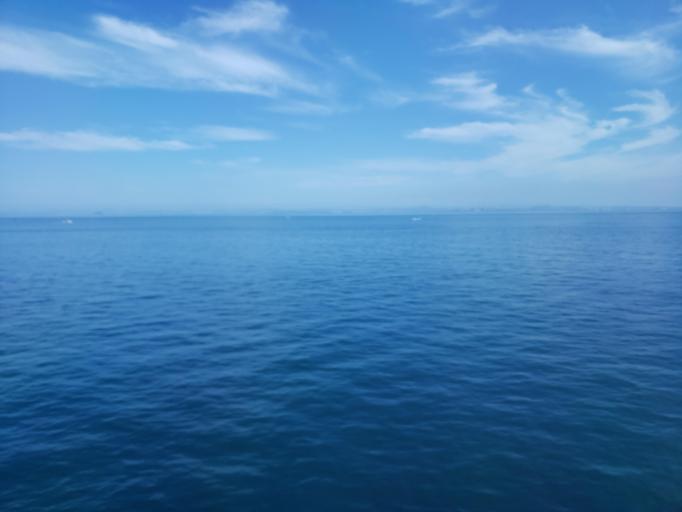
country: JP
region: Hyogo
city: Akashi
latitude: 34.5735
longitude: 134.8342
